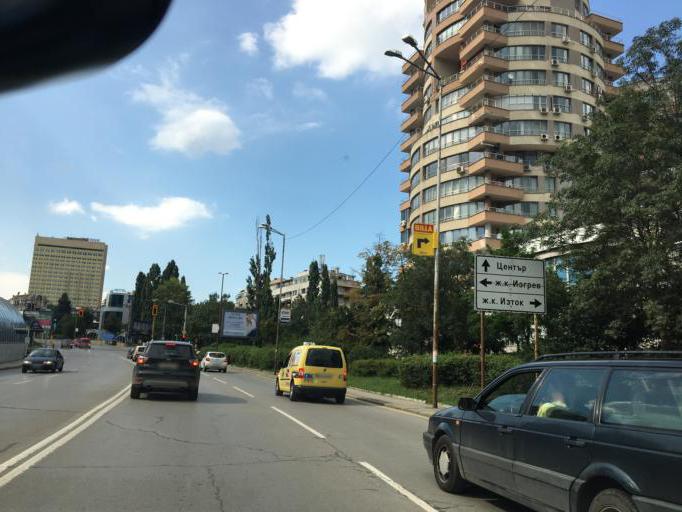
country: BG
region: Sofia-Capital
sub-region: Stolichna Obshtina
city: Sofia
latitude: 42.6704
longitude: 23.3520
